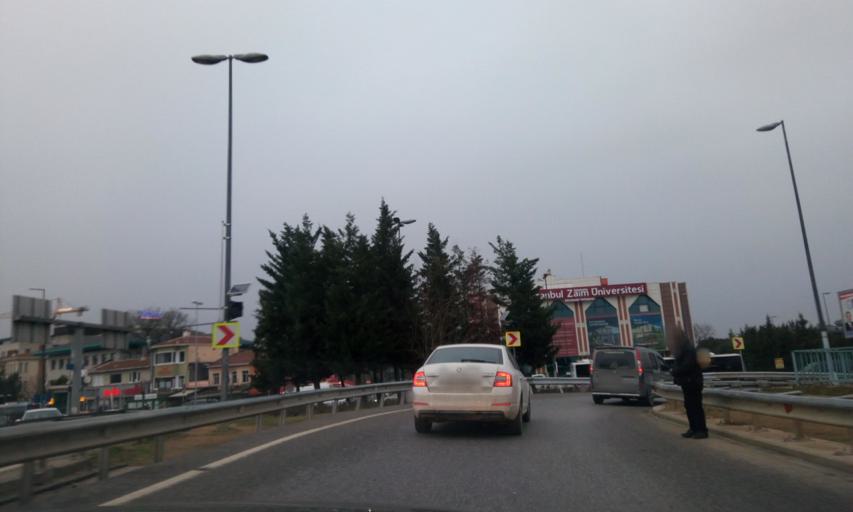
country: TR
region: Istanbul
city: UEskuedar
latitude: 41.0220
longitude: 29.0465
